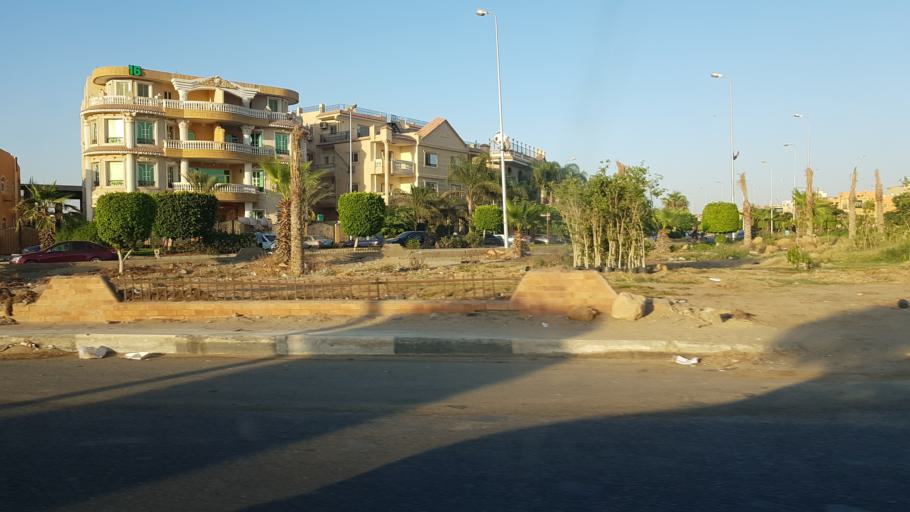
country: EG
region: Muhafazat al Qalyubiyah
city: Al Khankah
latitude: 30.0521
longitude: 31.4423
